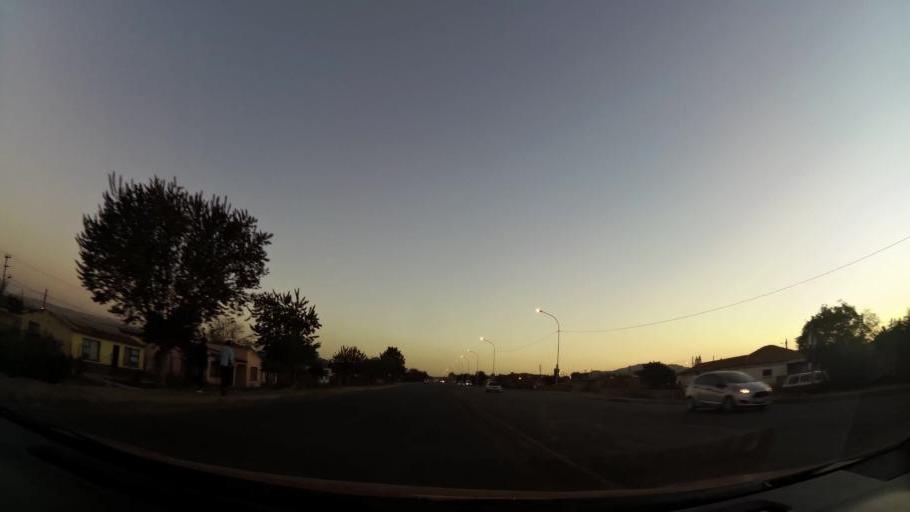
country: ZA
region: North-West
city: Ga-Rankuwa
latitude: -25.5906
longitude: 27.9836
